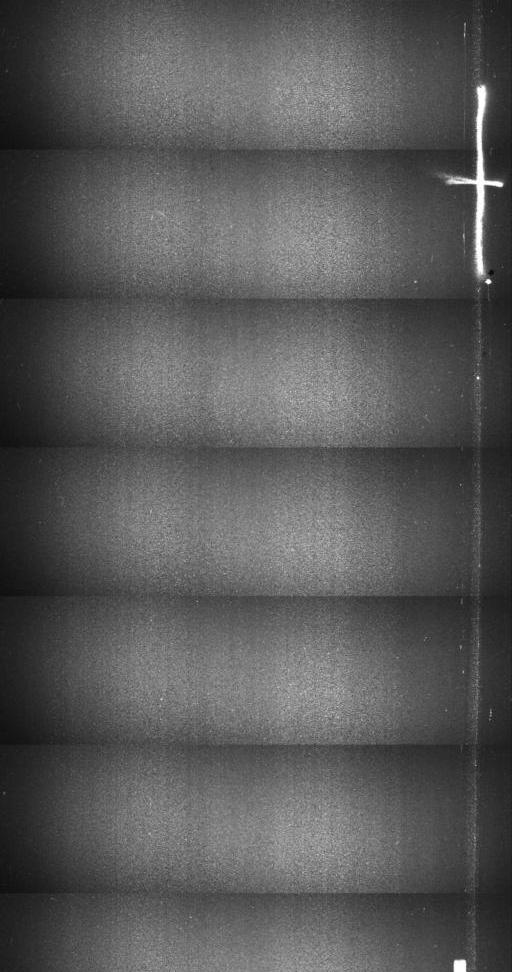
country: US
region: Vermont
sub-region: Windham County
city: Dover
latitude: 43.1082
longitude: -72.7961
